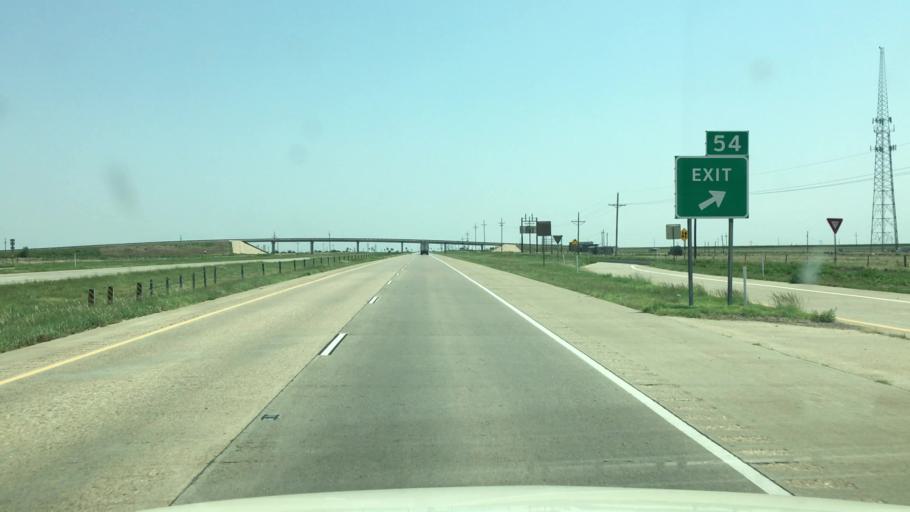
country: US
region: Texas
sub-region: Potter County
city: Bushland
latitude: 35.1971
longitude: -102.1200
